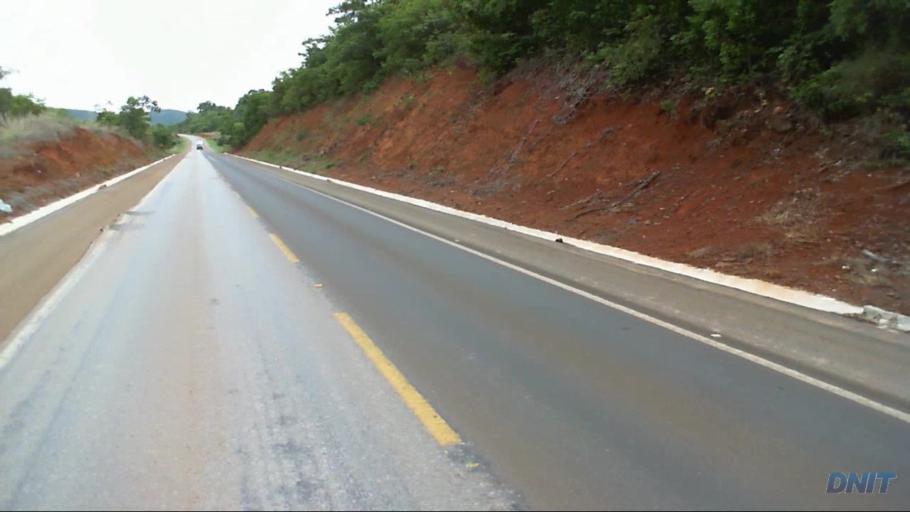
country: BR
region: Goias
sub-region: Barro Alto
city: Barro Alto
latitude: -14.9242
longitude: -48.9499
